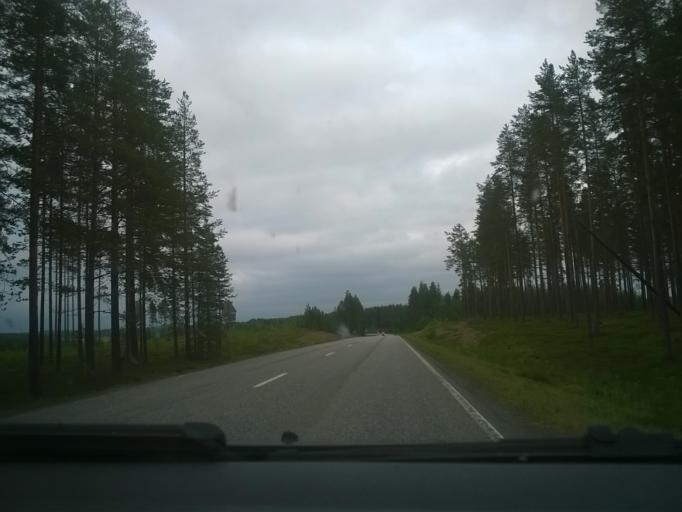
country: FI
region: Kainuu
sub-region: Kehys-Kainuu
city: Kuhmo
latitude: 64.1474
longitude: 29.4182
